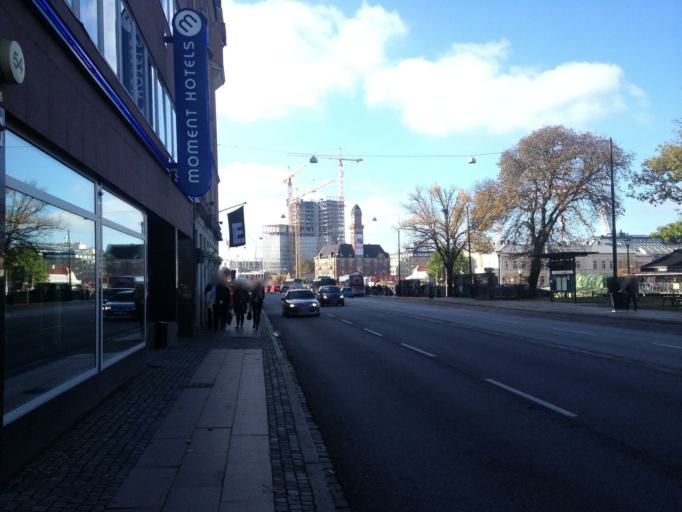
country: SE
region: Skane
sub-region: Malmo
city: Malmoe
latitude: 55.6078
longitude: 13.0018
